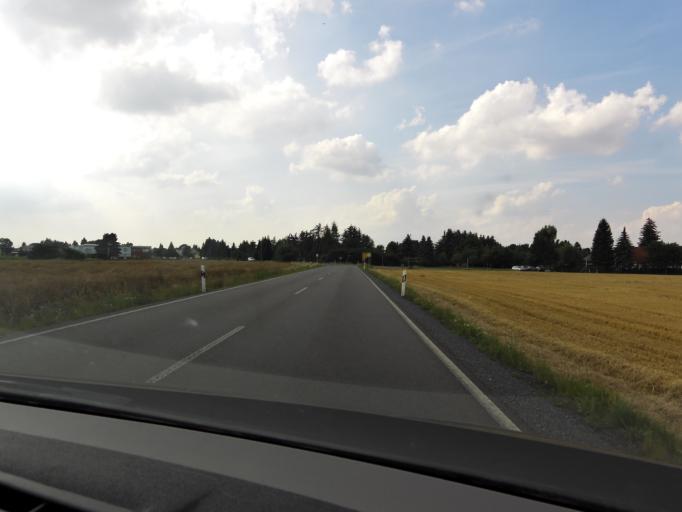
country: DE
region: Saxony
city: Naunhof
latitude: 51.2498
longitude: 12.5766
